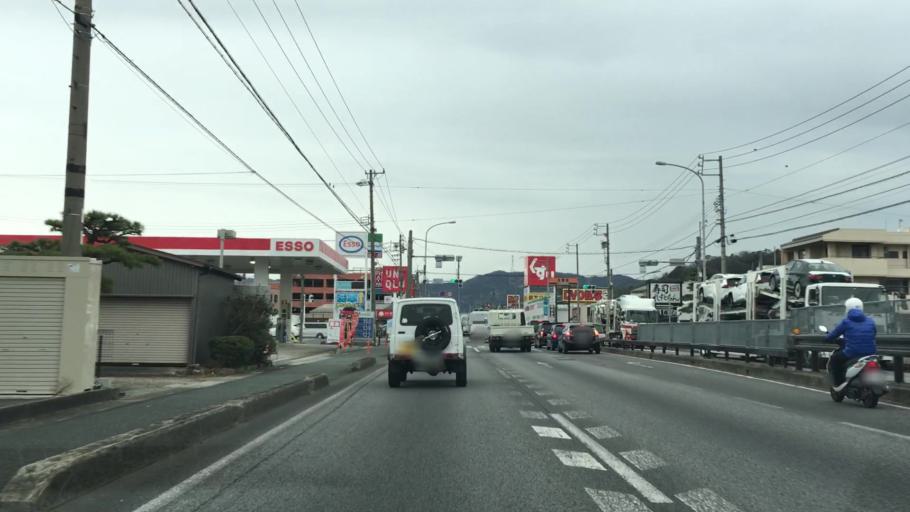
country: JP
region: Aichi
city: Kozakai-cho
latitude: 34.8425
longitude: 137.3234
